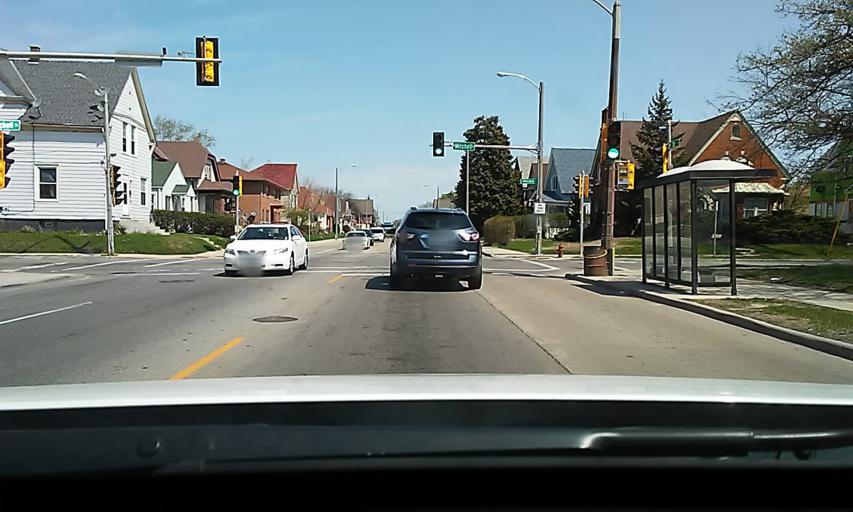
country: US
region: Wisconsin
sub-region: Milwaukee County
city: West Milwaukee
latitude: 43.0121
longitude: -87.9577
